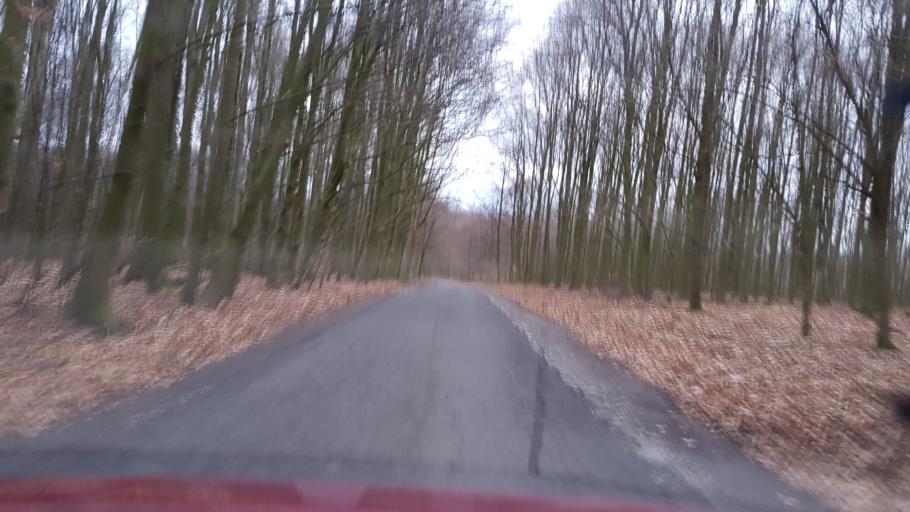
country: PL
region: West Pomeranian Voivodeship
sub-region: Powiat gryfinski
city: Stare Czarnowo
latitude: 53.3199
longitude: 14.7103
